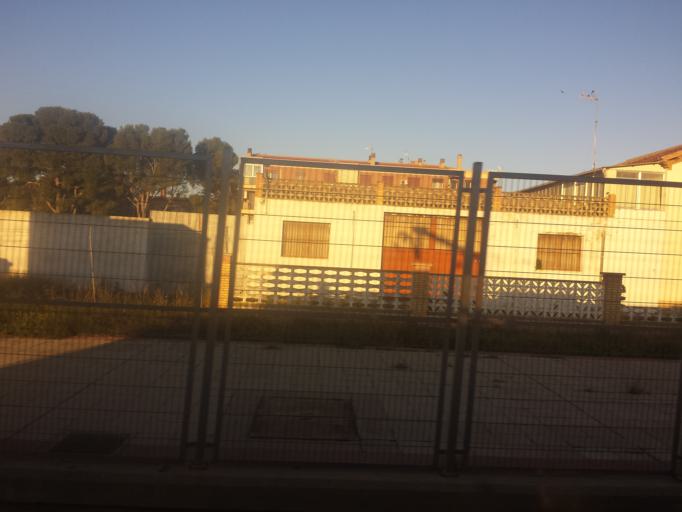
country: ES
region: Aragon
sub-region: Provincia de Zaragoza
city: Villanueva de Gallego
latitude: 41.7652
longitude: -0.8223
